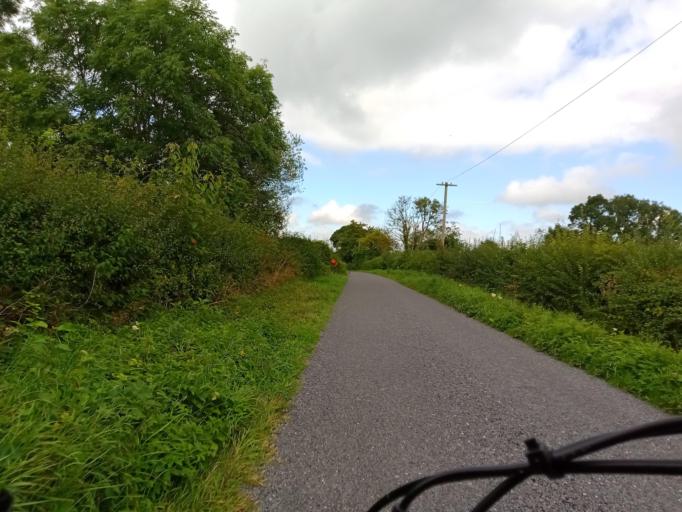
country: IE
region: Leinster
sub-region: Kilkenny
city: Callan
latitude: 52.5344
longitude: -7.2869
